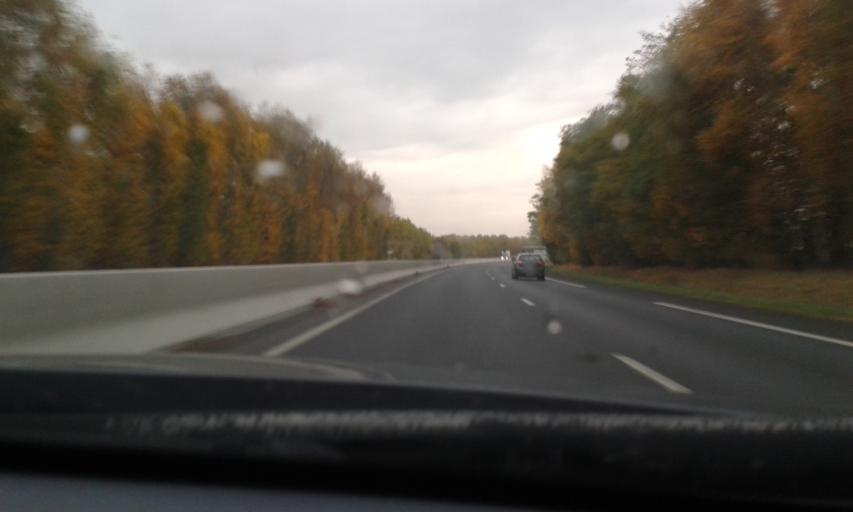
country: FR
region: Haute-Normandie
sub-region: Departement de la Seine-Maritime
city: Saint-Martin-Osmonville
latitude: 49.6243
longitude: 1.2619
